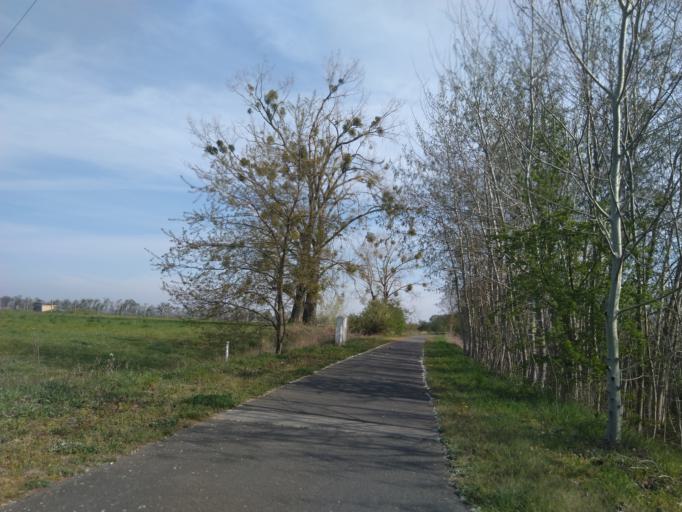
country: DE
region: Brandenburg
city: Wriezen
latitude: 52.7258
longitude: 14.1459
